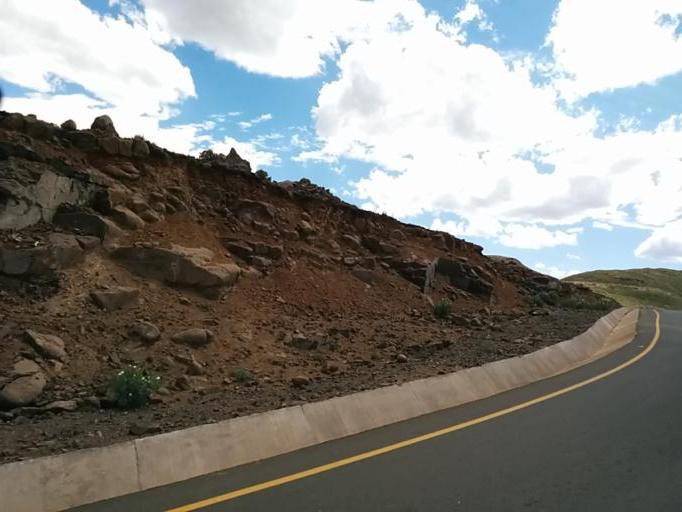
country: LS
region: Maseru
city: Nako
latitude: -29.9670
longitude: 28.1667
